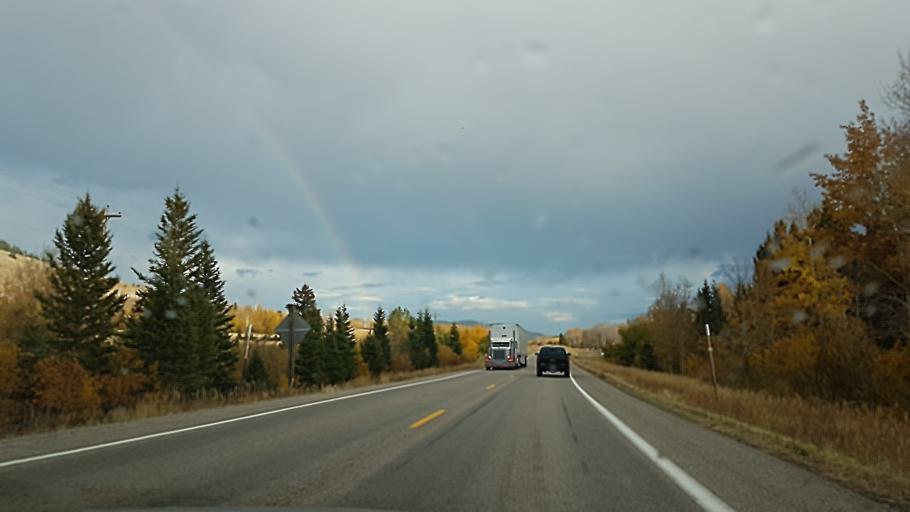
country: US
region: Montana
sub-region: Gallatin County
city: West Yellowstone
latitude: 44.6717
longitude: -111.4036
